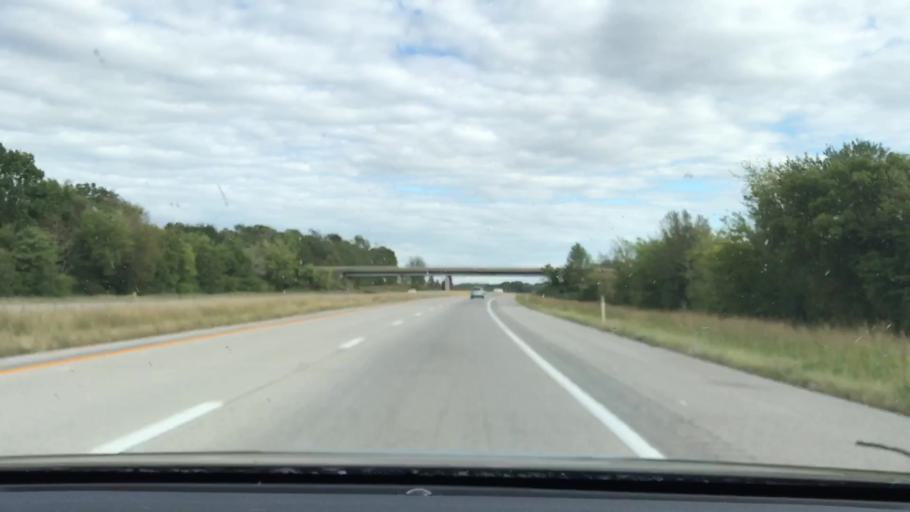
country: US
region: Kentucky
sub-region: Christian County
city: Hopkinsville
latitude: 36.7884
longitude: -87.5876
